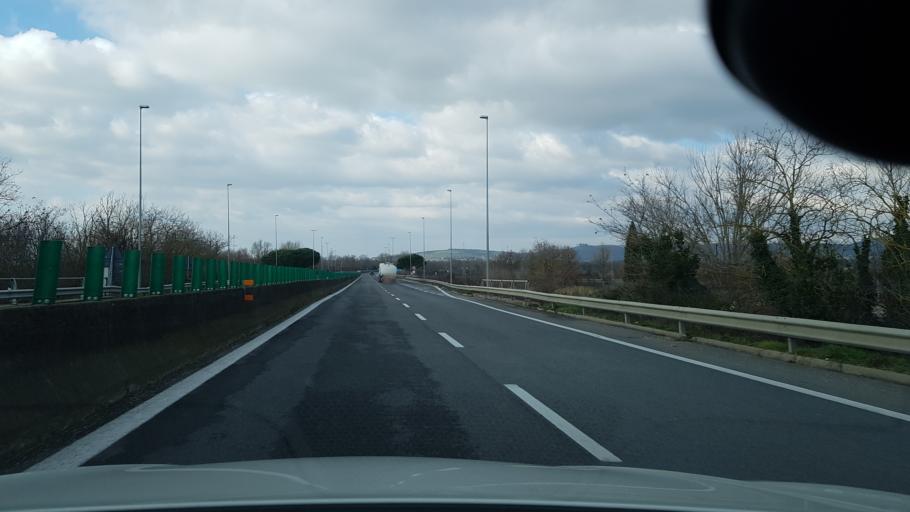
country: IT
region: Umbria
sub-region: Provincia di Perugia
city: Passignano sul Trasimeno
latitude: 43.1958
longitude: 12.1102
